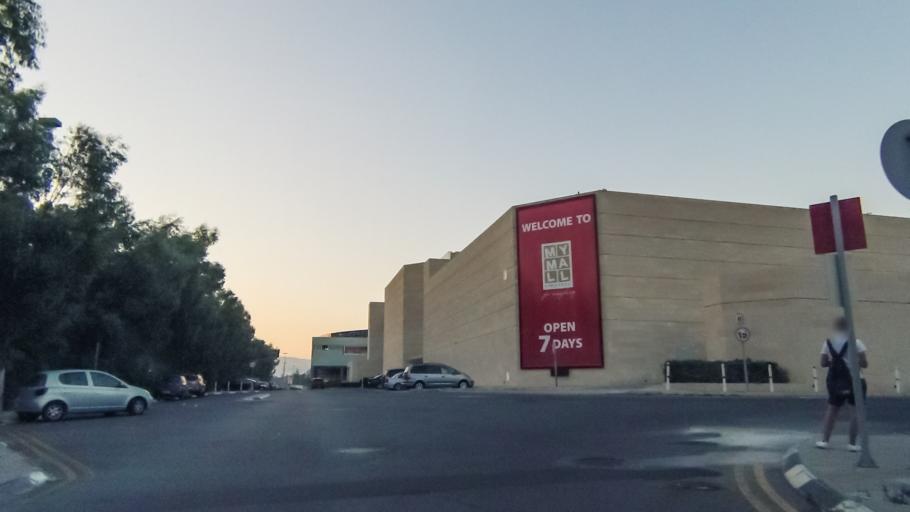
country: CY
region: Limassol
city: Ypsonas
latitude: 34.6508
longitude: 32.9972
